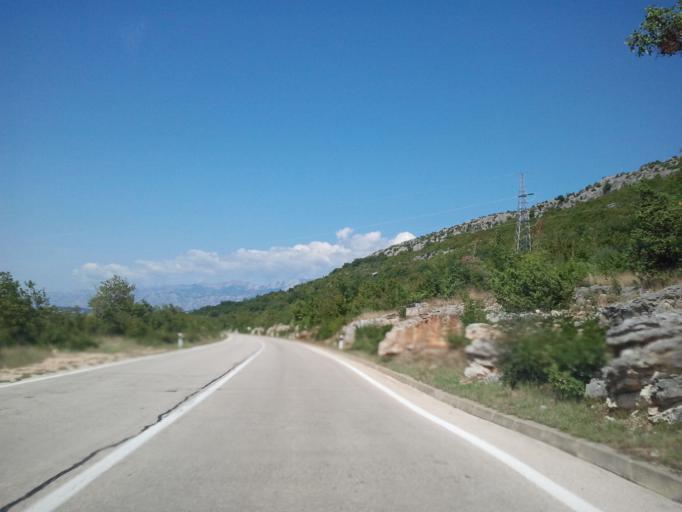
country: HR
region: Zadarska
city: Krusevo
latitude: 44.1690
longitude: 15.6248
